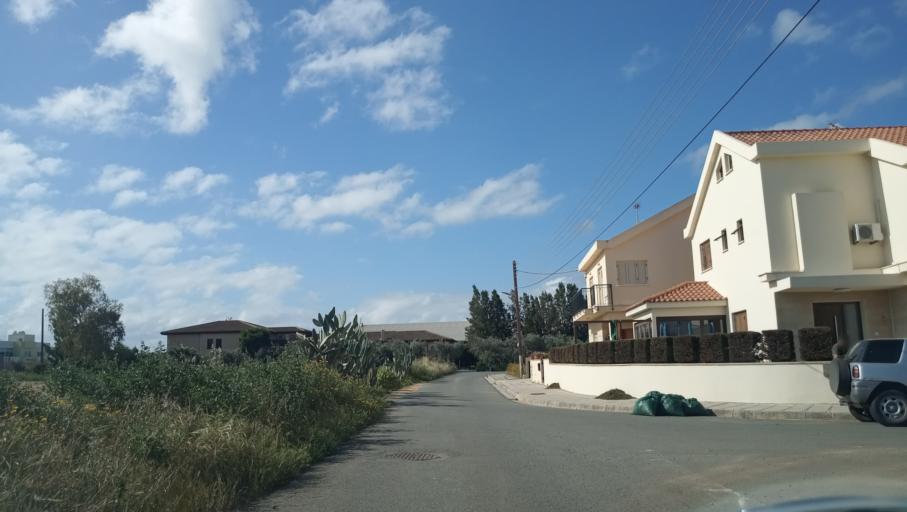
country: CY
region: Lefkosia
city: Tseri
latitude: 35.1107
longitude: 33.3317
